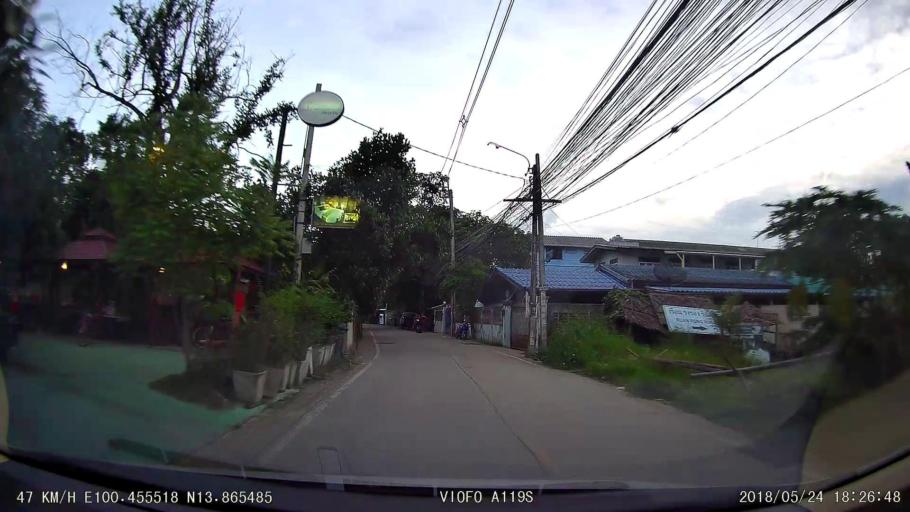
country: TH
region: Nonthaburi
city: Bang Bua Thong
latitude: 13.8655
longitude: 100.4556
